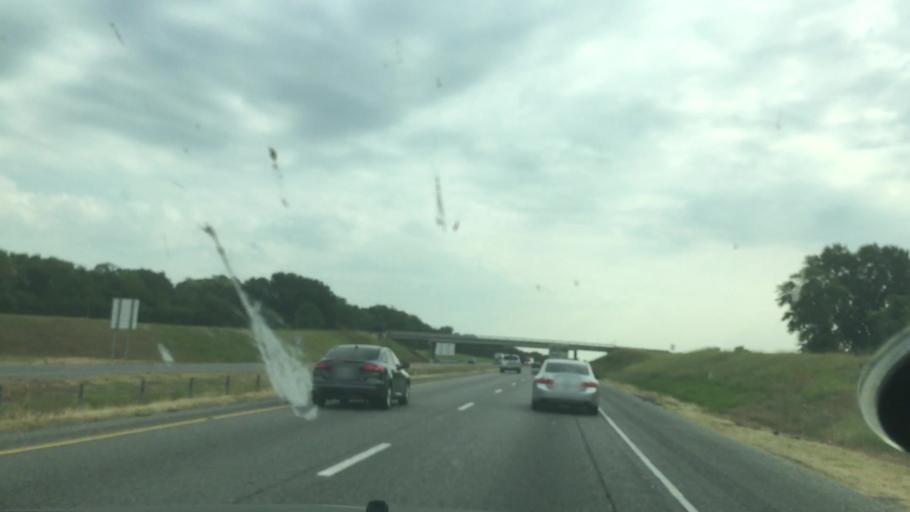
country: US
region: Oklahoma
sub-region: Bryan County
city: Colbert
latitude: 33.8293
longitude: -96.5281
